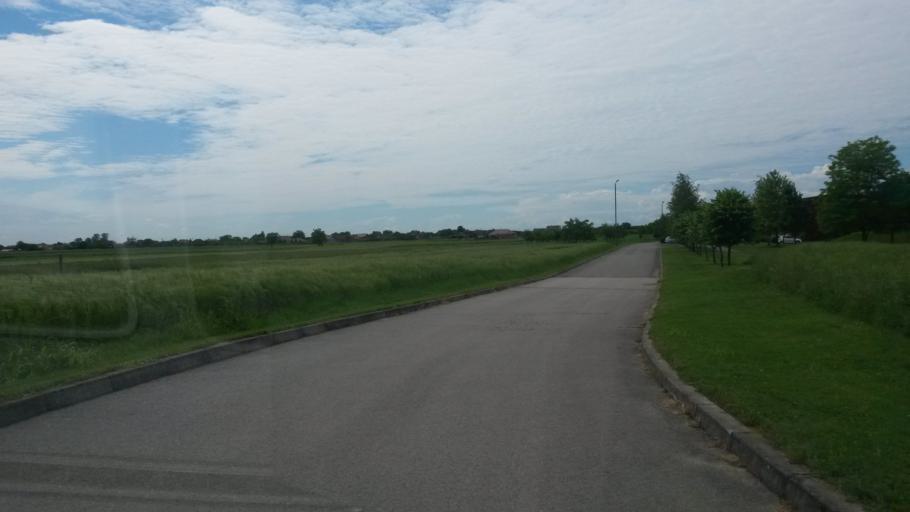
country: HR
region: Vukovarsko-Srijemska
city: Vodinci
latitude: 45.2825
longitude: 18.6148
